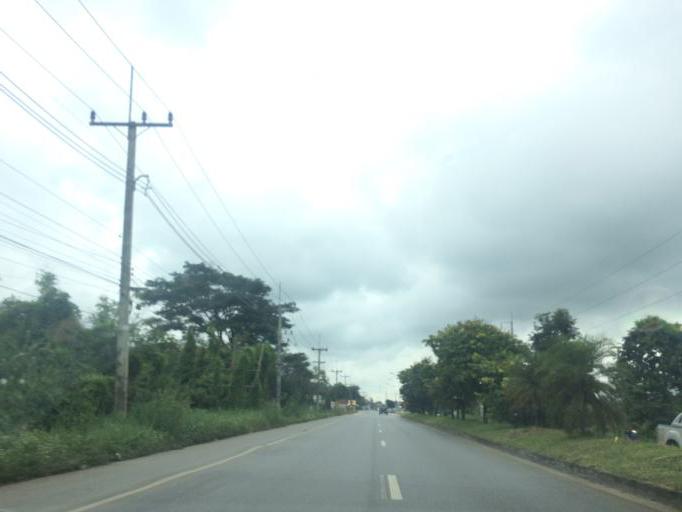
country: TH
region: Chiang Rai
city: Mae Chan
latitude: 20.0685
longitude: 99.8756
